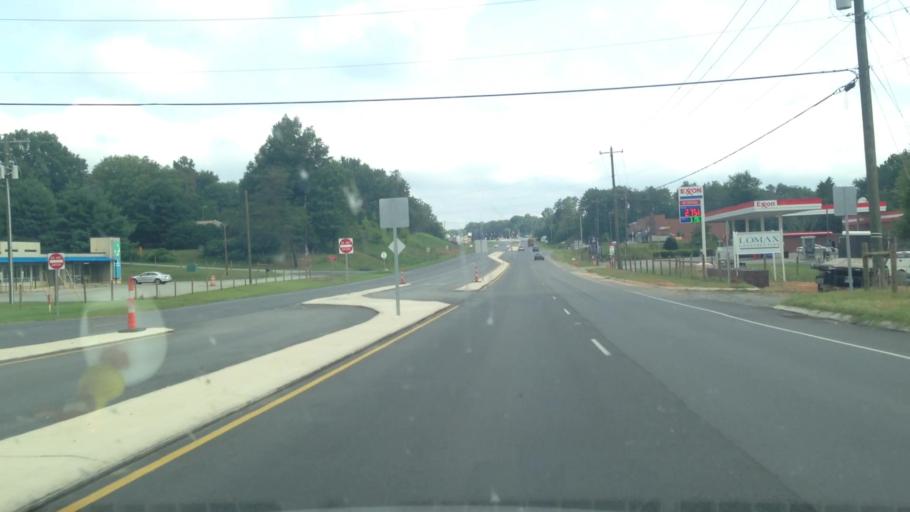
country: US
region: North Carolina
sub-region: Guilford County
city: Summerfield
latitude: 36.1859
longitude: -79.8890
